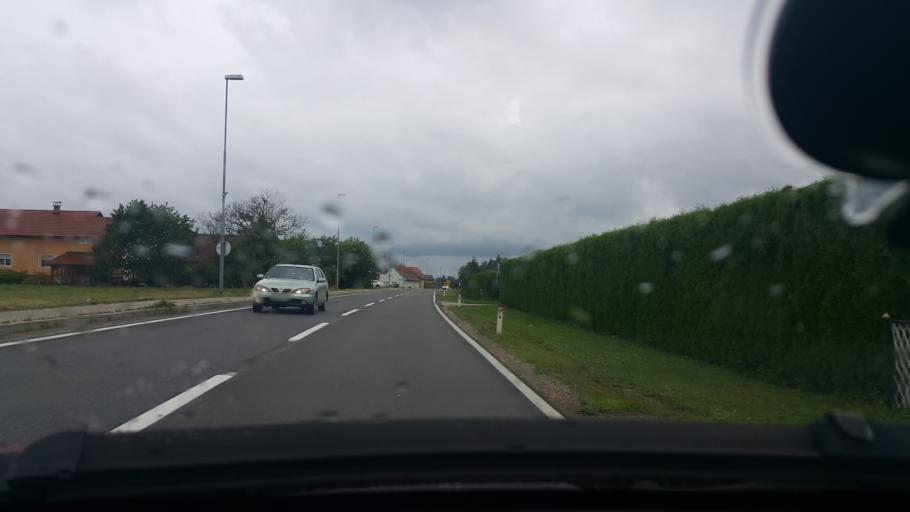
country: SI
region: Gorisnica
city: Gorisnica
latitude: 46.4148
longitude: 16.0062
